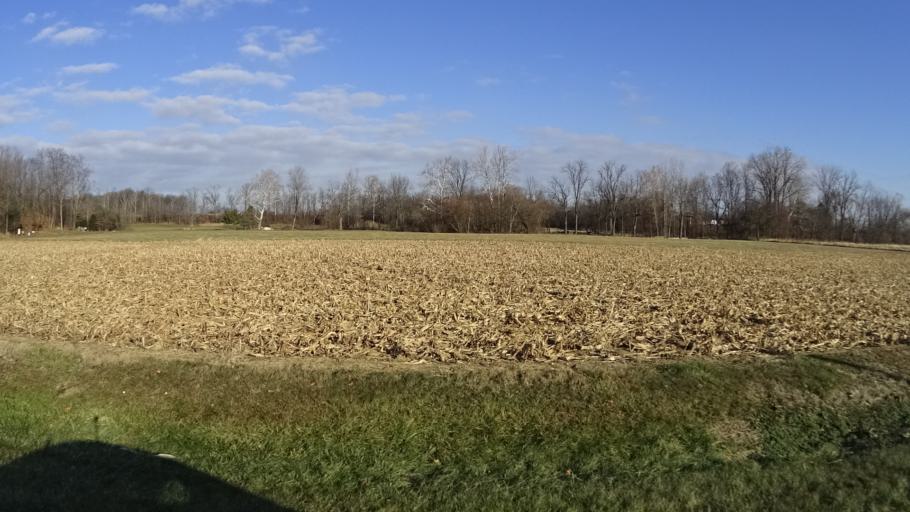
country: US
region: Ohio
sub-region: Lorain County
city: Oberlin
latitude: 41.2653
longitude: -82.1859
